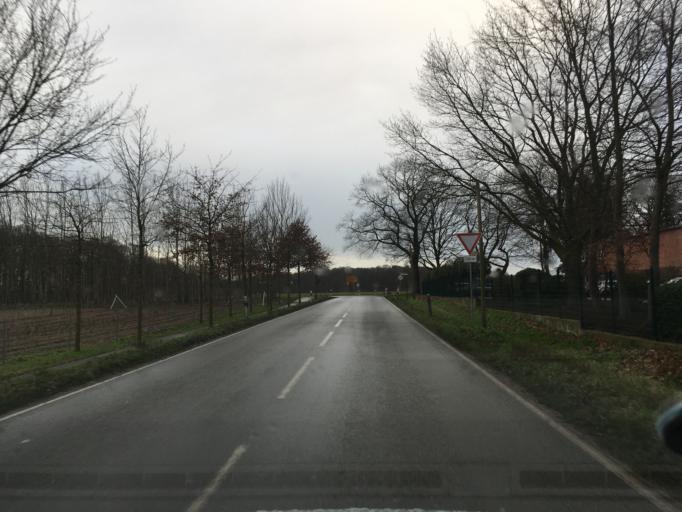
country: DE
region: North Rhine-Westphalia
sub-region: Regierungsbezirk Munster
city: Schoppingen
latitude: 52.0876
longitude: 7.2154
